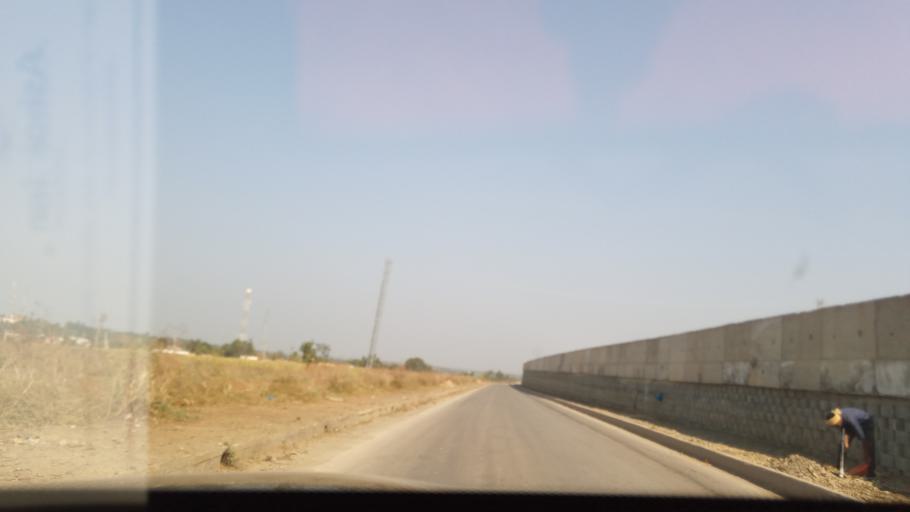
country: IN
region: Karnataka
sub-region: Haveri
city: Savanur
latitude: 14.9178
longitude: 75.2731
